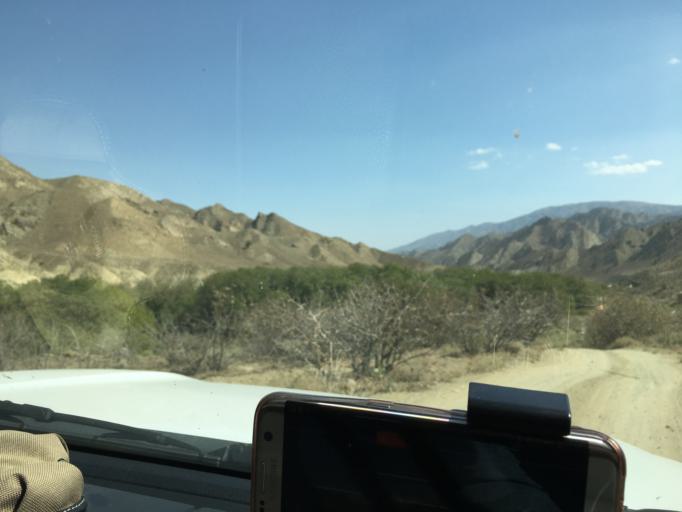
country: TM
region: Ahal
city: Baharly
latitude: 38.3493
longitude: 57.1021
